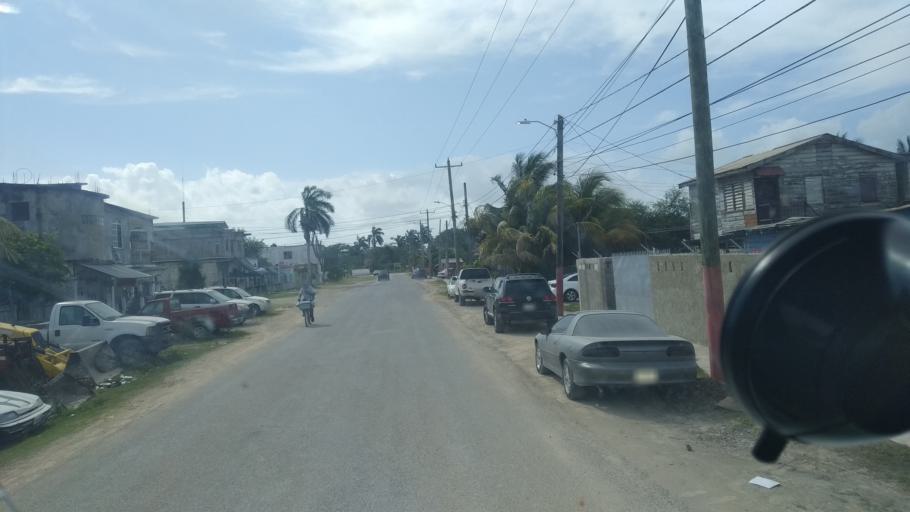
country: BZ
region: Corozal
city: Corozal
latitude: 18.3991
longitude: -88.3815
